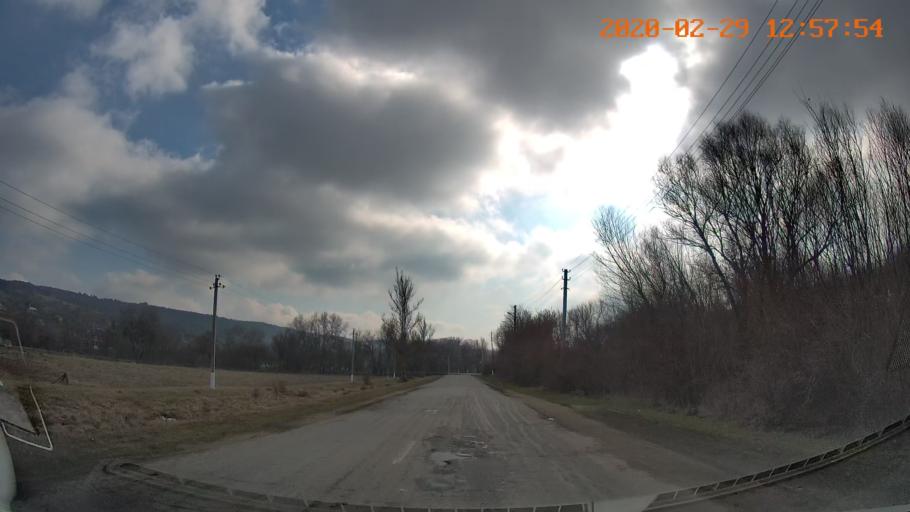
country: MD
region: Telenesti
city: Camenca
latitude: 48.0734
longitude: 28.7173
